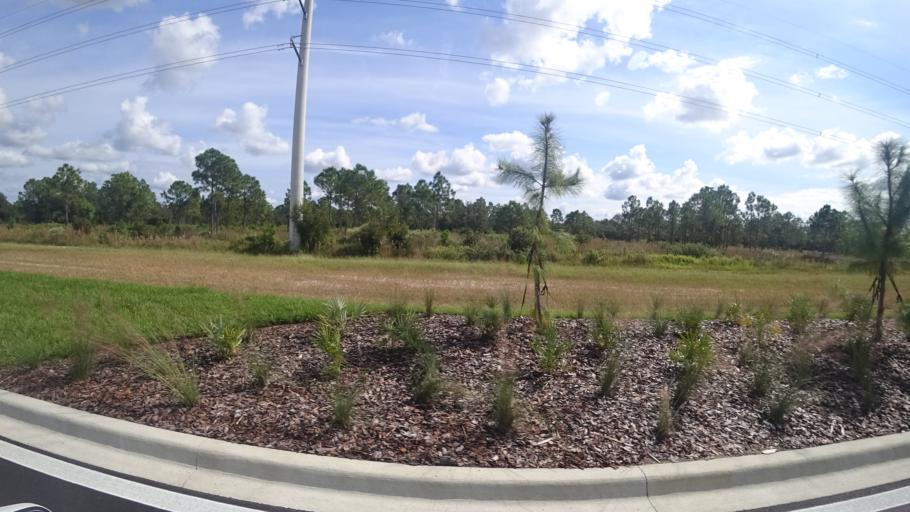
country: US
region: Florida
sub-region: Sarasota County
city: The Meadows
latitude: 27.4044
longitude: -82.3542
